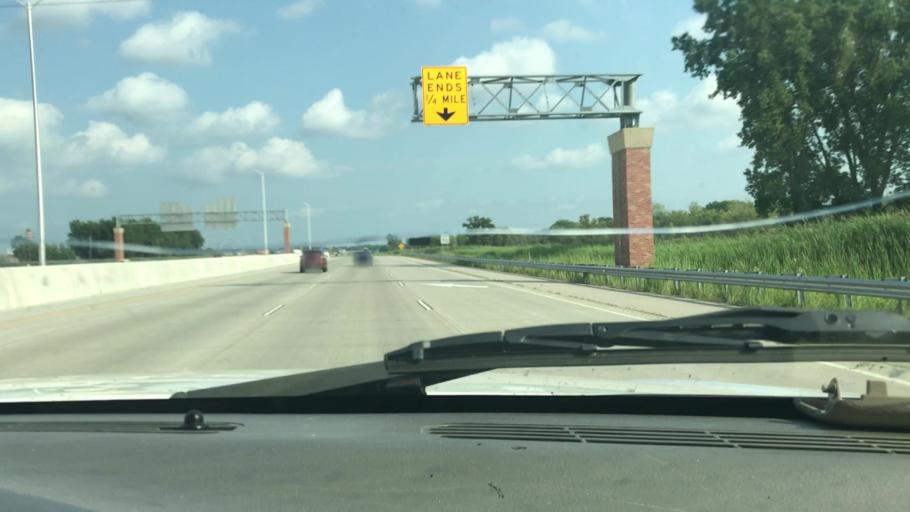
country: US
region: Wisconsin
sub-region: Brown County
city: Green Bay
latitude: 44.5514
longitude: -88.0410
